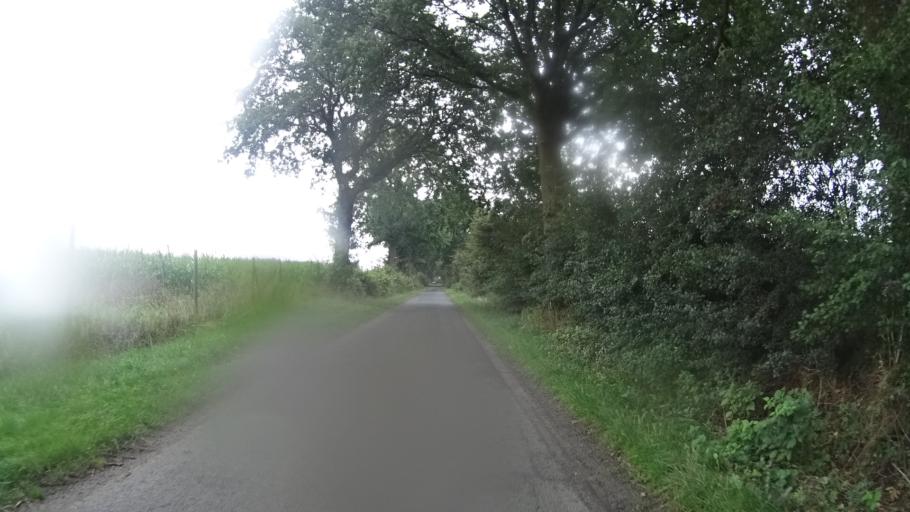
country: DE
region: Schleswig-Holstein
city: Bilsen
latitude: 53.7722
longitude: 9.8633
